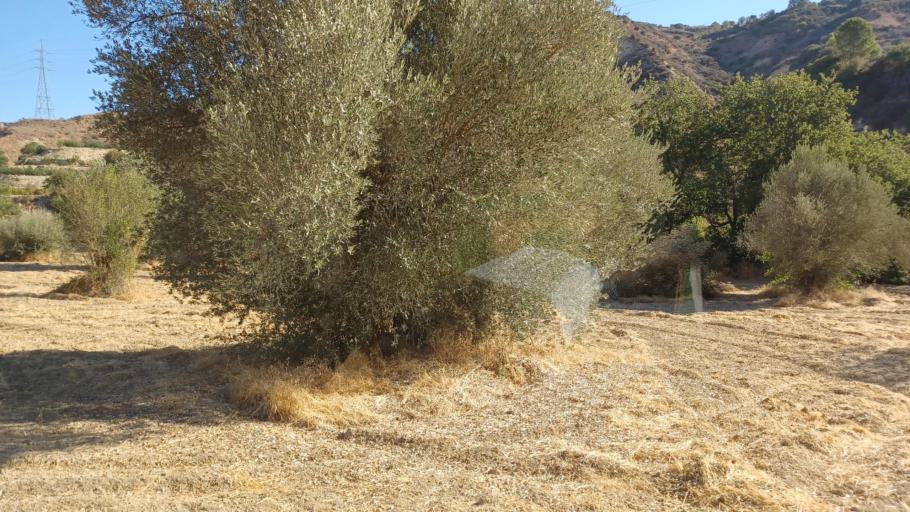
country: CY
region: Pafos
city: Polis
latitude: 34.9393
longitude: 32.4767
